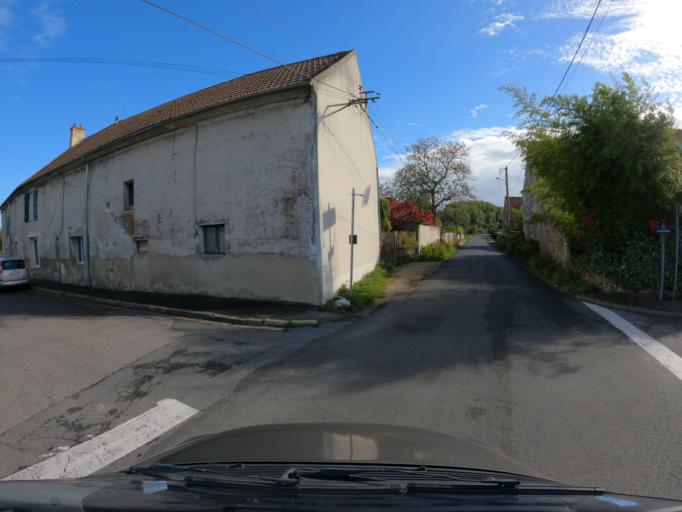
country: FR
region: Ile-de-France
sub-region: Departement de Seine-et-Marne
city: Saint-Germain-sur-Morin
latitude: 48.8797
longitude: 2.8540
